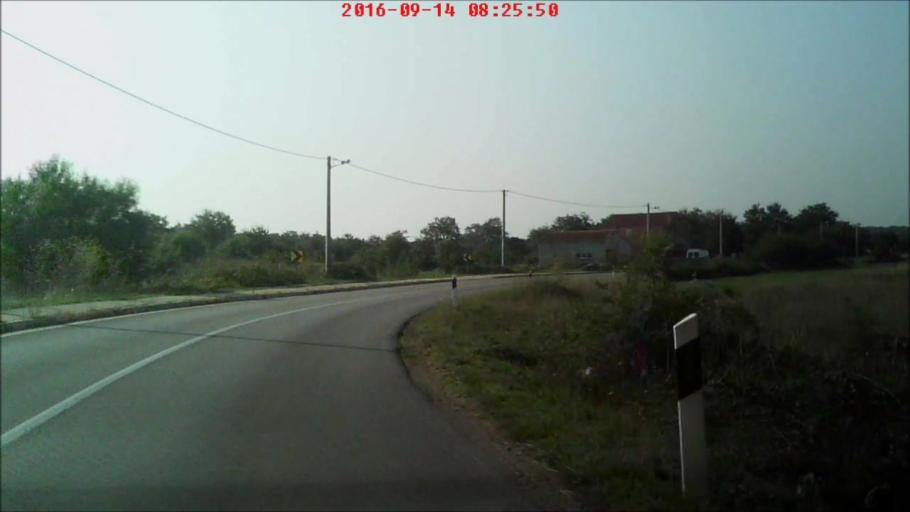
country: HR
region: Zadarska
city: Vrsi
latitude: 44.2007
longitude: 15.2571
